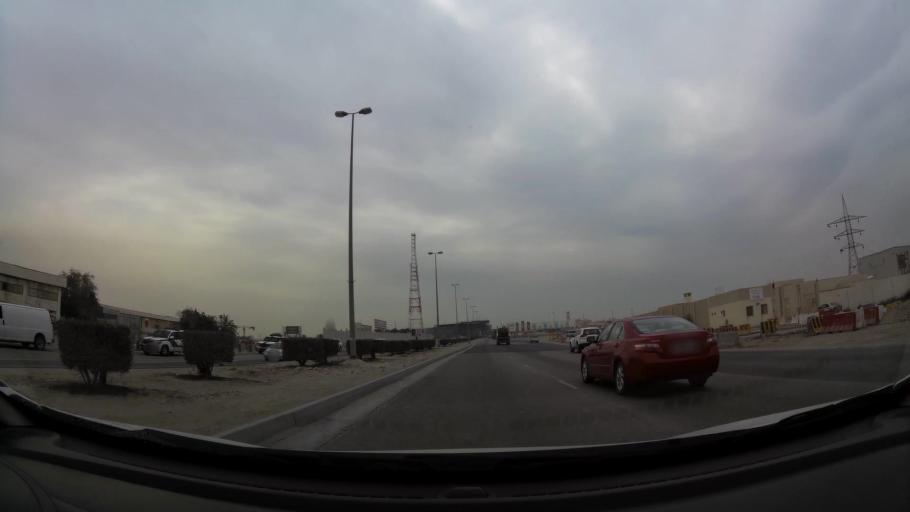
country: BH
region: Northern
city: Sitrah
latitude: 26.1263
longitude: 50.5953
